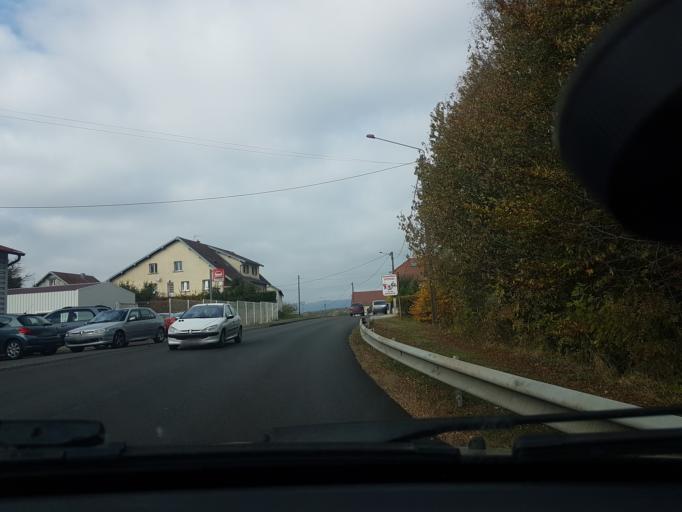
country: FR
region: Franche-Comte
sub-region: Departement de la Haute-Saone
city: Frahier-et-Chatebier
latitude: 47.6551
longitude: 6.7520
